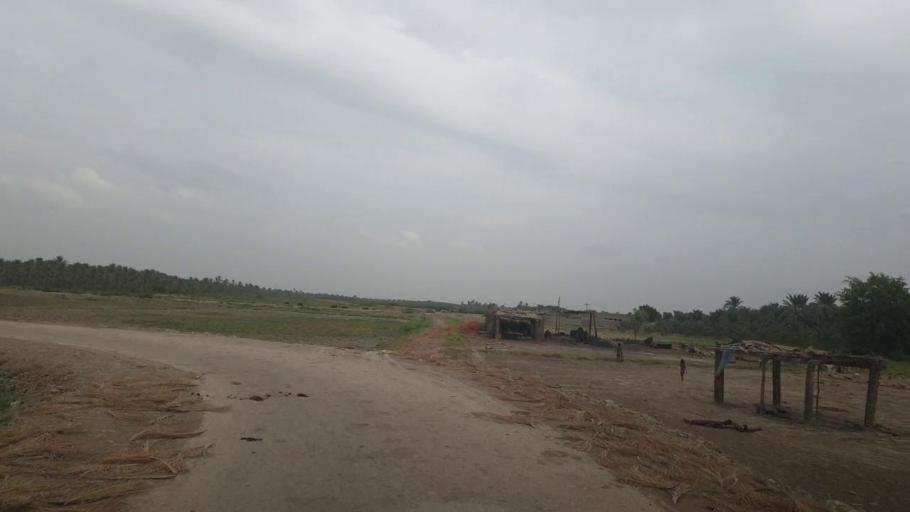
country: PK
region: Sindh
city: Khairpur
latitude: 27.5749
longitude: 68.7306
